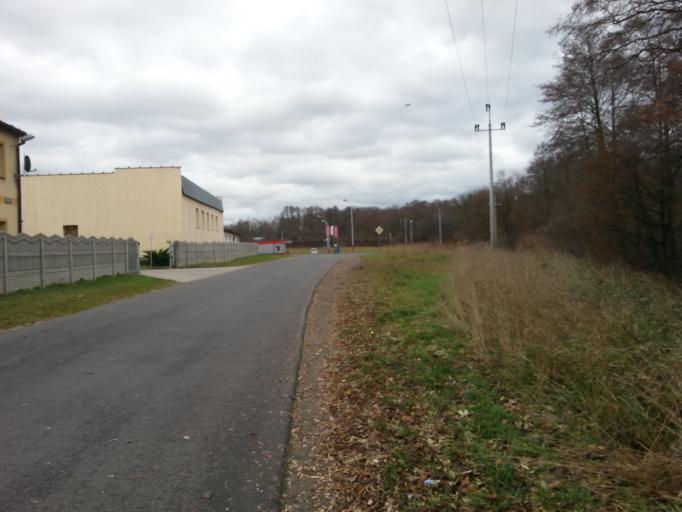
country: PL
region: Lower Silesian Voivodeship
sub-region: Powiat olesnicki
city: Twardogora
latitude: 51.3636
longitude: 17.4739
